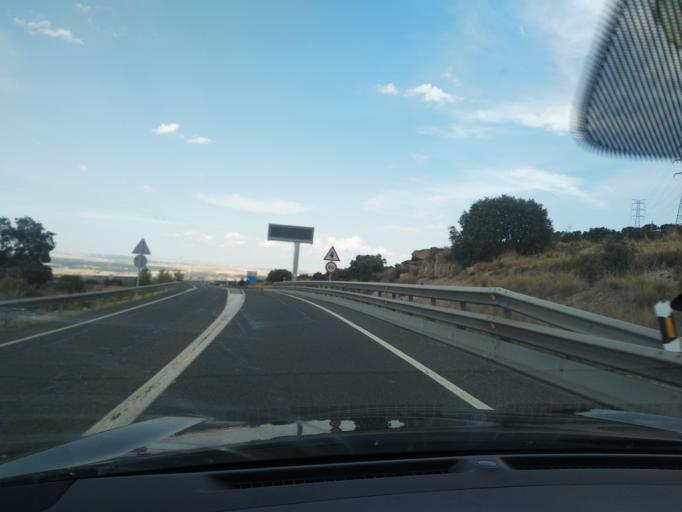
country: ES
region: Castille and Leon
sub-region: Provincia de Segovia
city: Otero de Herreros
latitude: 40.7873
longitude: -4.2132
